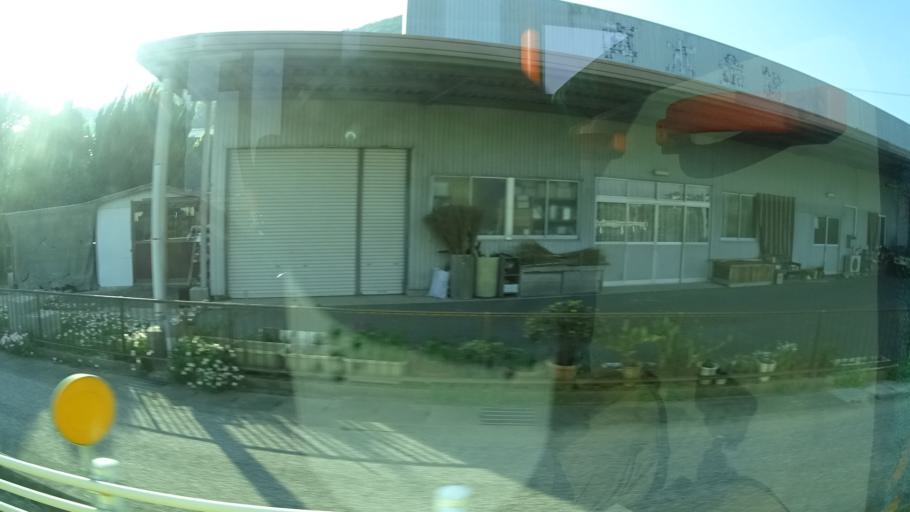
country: JP
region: Aichi
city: Tahara
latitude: 34.6511
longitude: 137.2262
